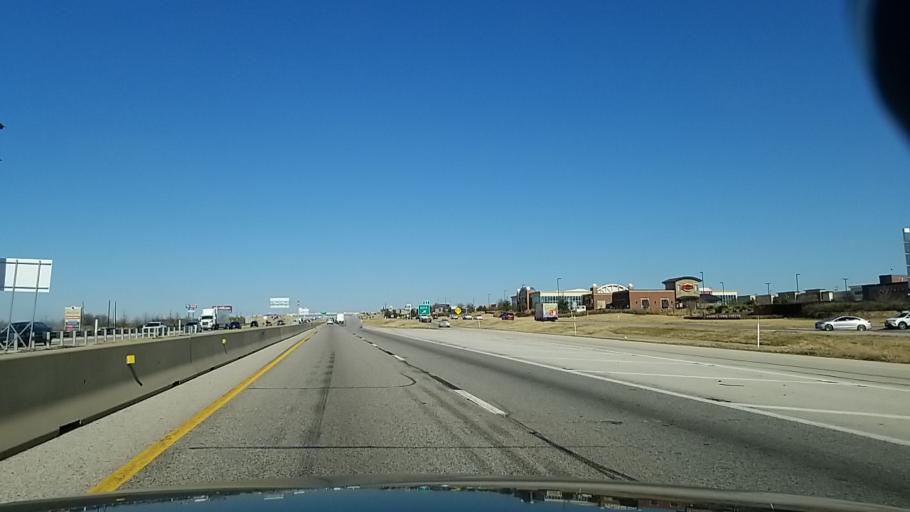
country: US
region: Texas
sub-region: Tarrant County
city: Blue Mound
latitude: 32.9047
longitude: -97.3171
